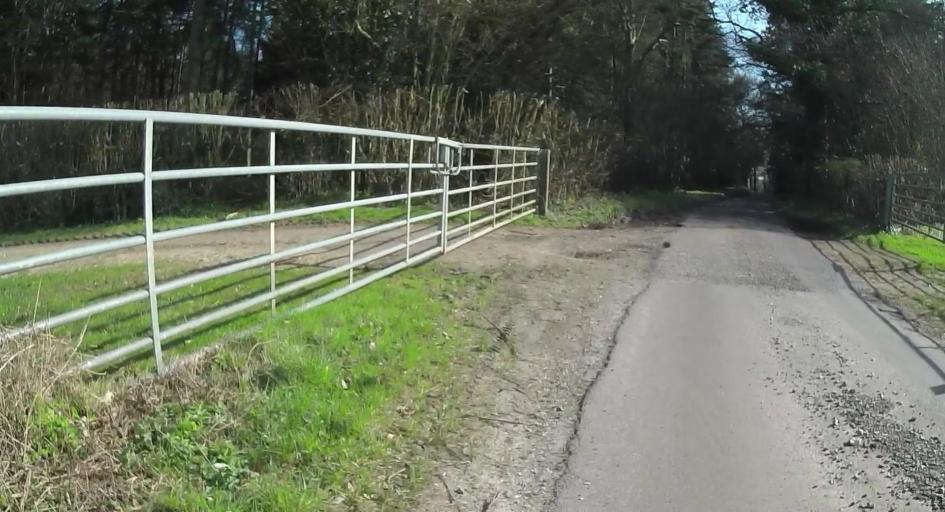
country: GB
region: England
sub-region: Hampshire
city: Highclere
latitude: 51.2549
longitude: -1.3671
